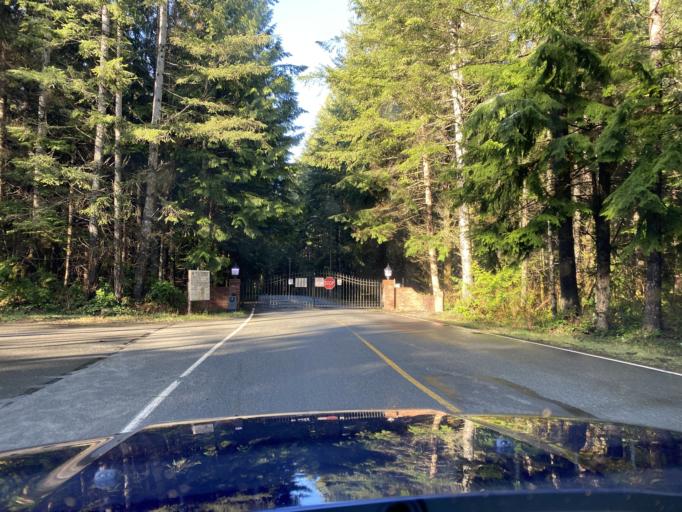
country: US
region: Washington
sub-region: King County
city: Fall City
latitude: 47.5129
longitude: -121.8946
